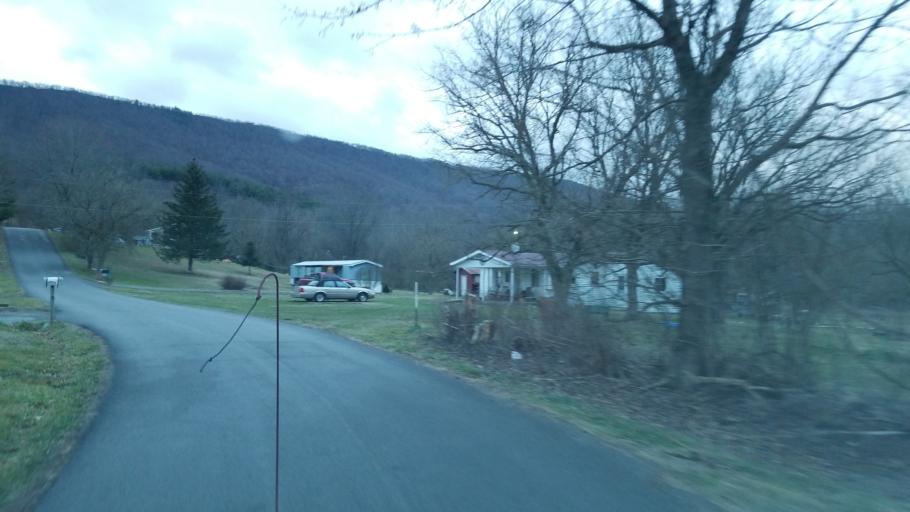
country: US
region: Virginia
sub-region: Pulaski County
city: Pulaski
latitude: 37.1601
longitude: -80.8674
